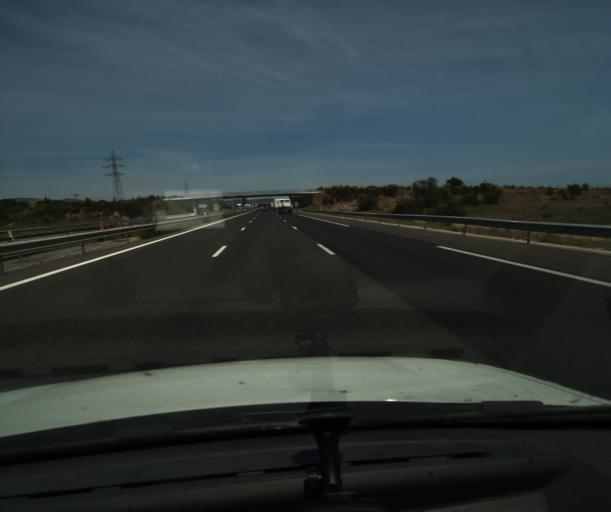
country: FR
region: Languedoc-Roussillon
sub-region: Departement des Pyrenees-Orientales
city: Salses-le-Chateau
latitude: 42.8023
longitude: 2.8991
